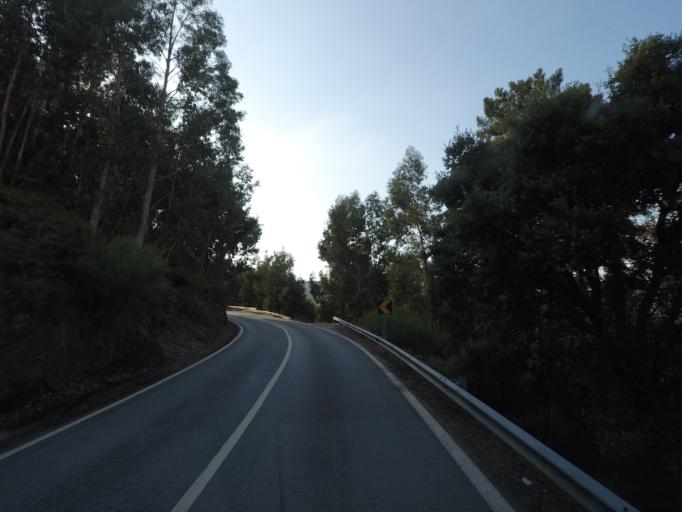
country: PT
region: Vila Real
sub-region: Mesao Frio
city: Mesao Frio
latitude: 41.1759
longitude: -7.9180
